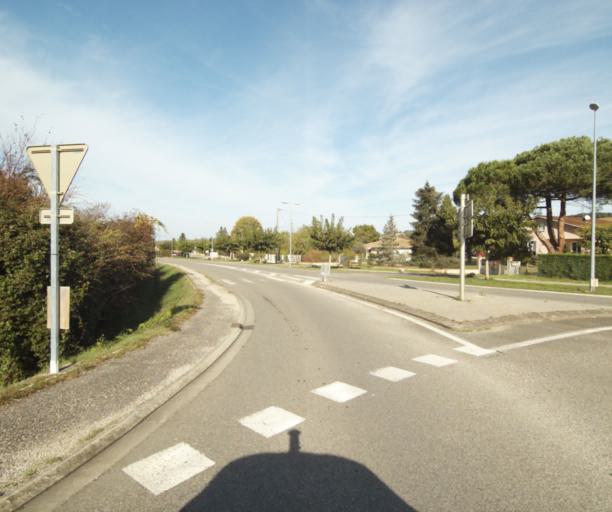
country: FR
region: Midi-Pyrenees
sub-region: Departement du Tarn-et-Garonne
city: Nohic
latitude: 43.9080
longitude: 1.4497
